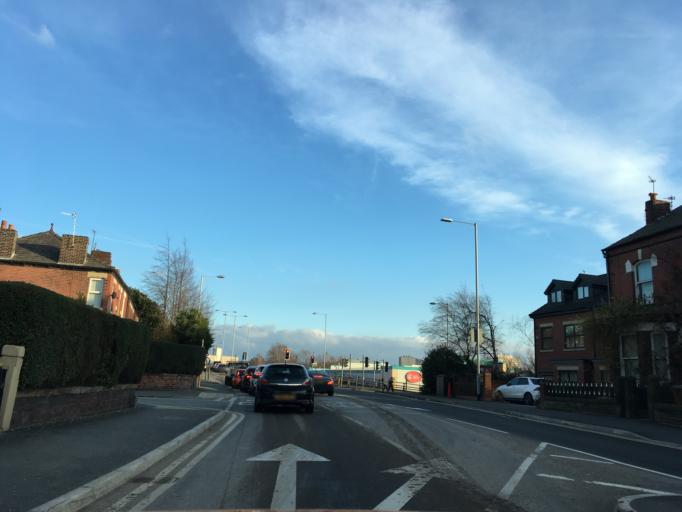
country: GB
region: England
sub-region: Borough of Stockport
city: Cheadle Heath
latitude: 53.4099
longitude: -2.1783
